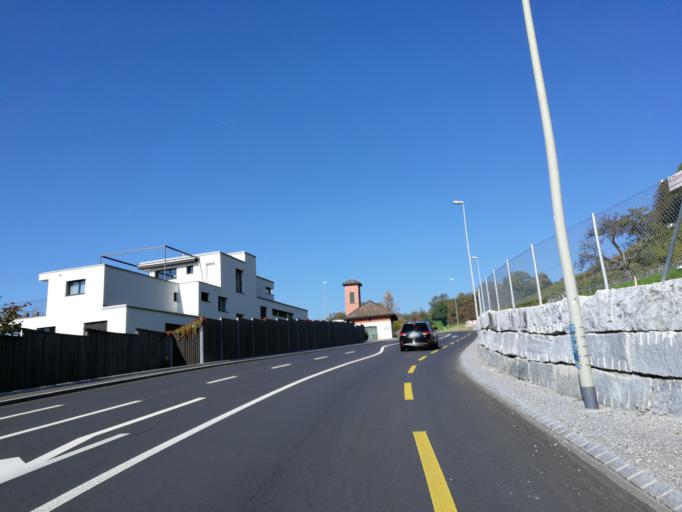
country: CH
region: Zurich
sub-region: Bezirk Meilen
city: Stafa
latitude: 47.2482
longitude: 8.7266
